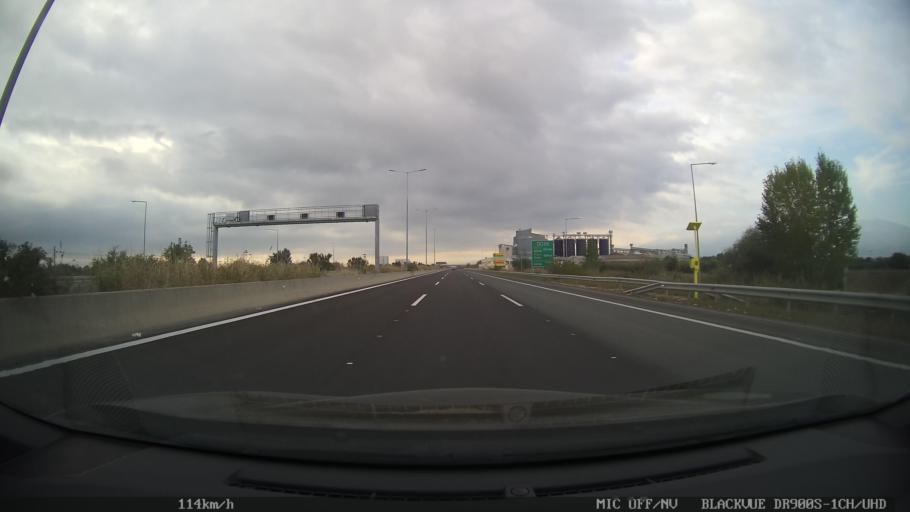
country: GR
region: Central Macedonia
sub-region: Nomos Pierias
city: Peristasi
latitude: 40.2506
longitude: 22.5331
